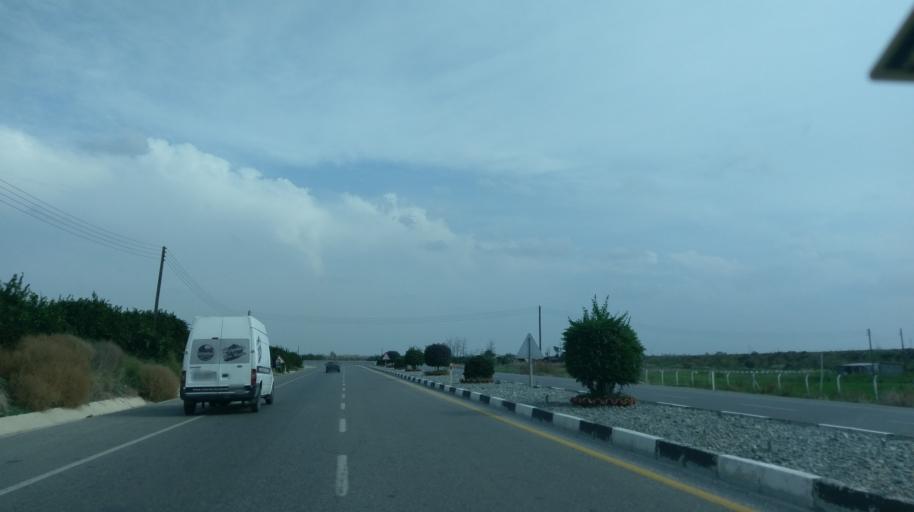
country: CY
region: Lefkosia
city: Morfou
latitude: 35.1973
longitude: 33.0149
